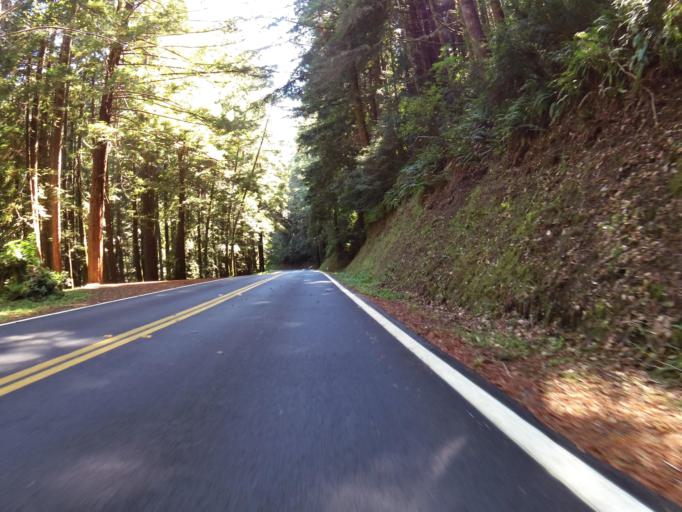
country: US
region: California
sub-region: Humboldt County
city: Redway
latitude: 39.7974
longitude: -123.8199
